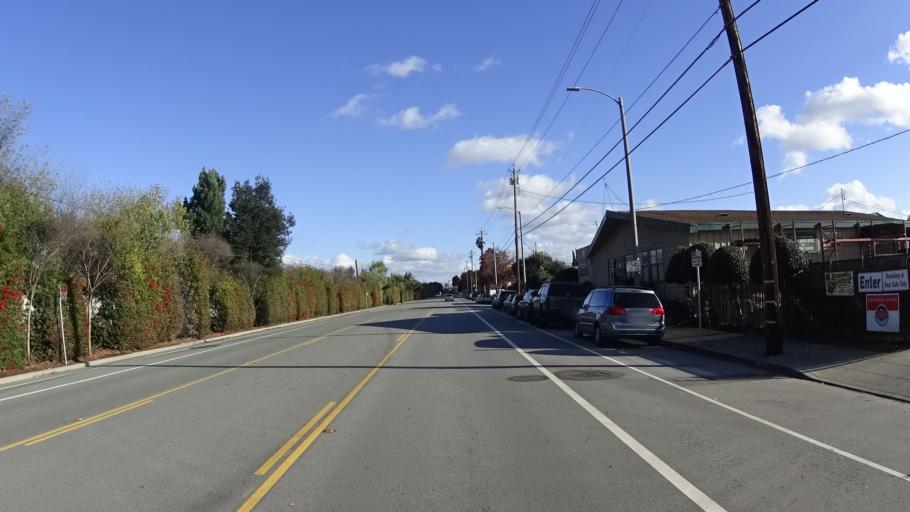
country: US
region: California
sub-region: Santa Clara County
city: Sunnyvale
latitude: 37.3816
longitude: -122.0405
